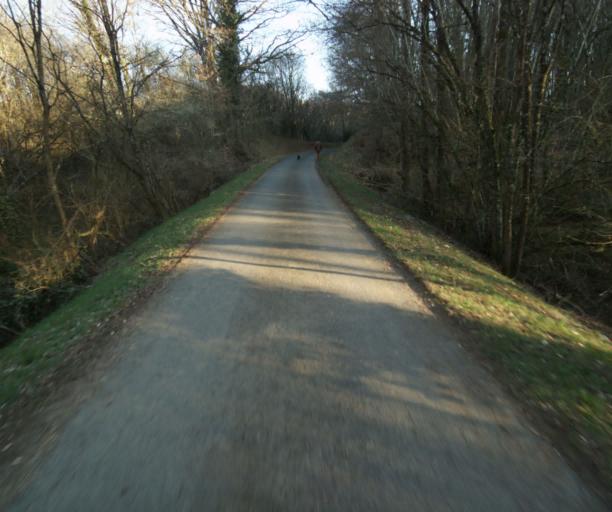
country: FR
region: Limousin
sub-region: Departement de la Correze
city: Saint-Clement
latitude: 45.3503
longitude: 1.6707
